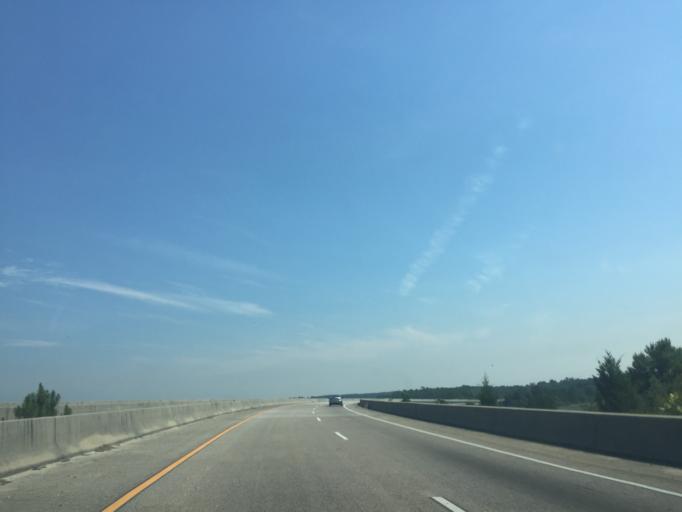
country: US
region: Georgia
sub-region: Chatham County
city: Georgetown
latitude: 31.9990
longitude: -81.2009
